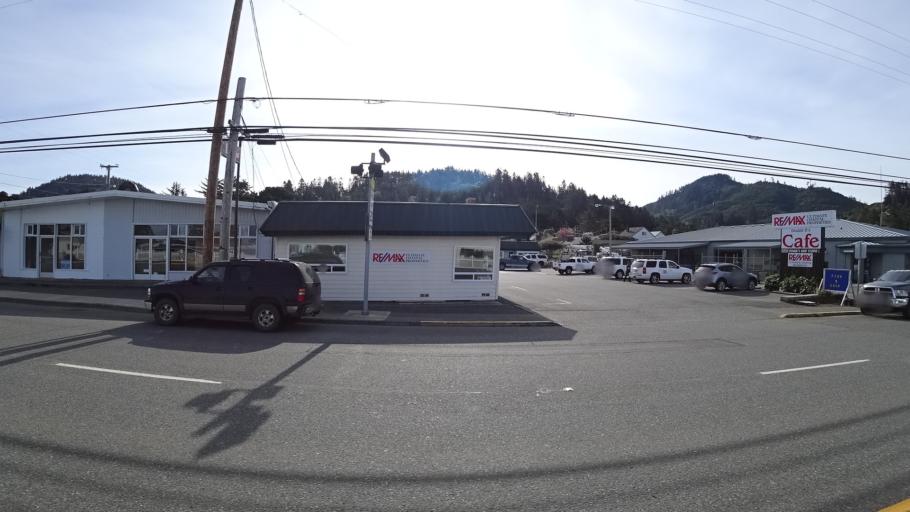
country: US
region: Oregon
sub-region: Curry County
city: Gold Beach
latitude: 42.4071
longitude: -124.4210
